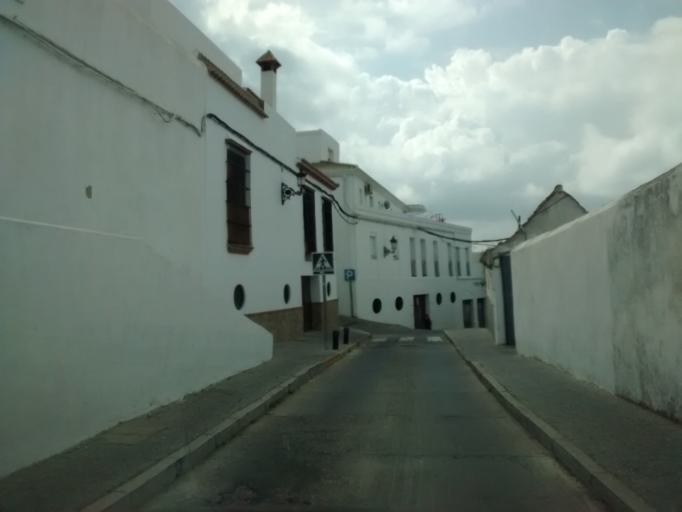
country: ES
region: Andalusia
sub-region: Provincia de Cadiz
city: Medina Sidonia
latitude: 36.4561
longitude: -5.9282
